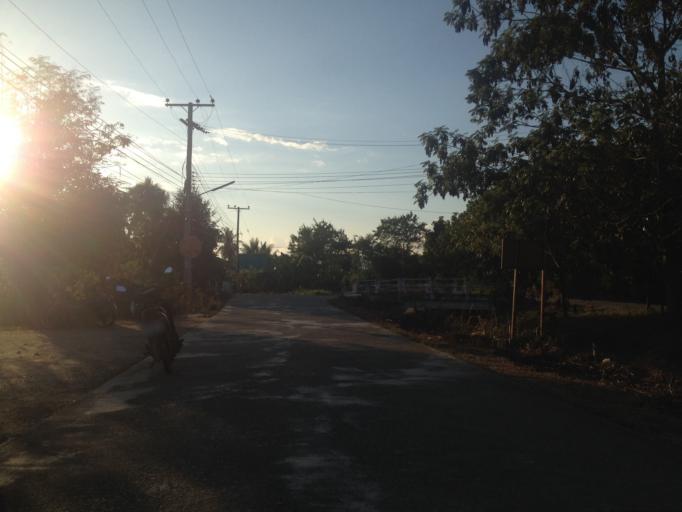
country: TH
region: Chiang Mai
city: San Pa Tong
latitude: 18.6495
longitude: 98.8882
